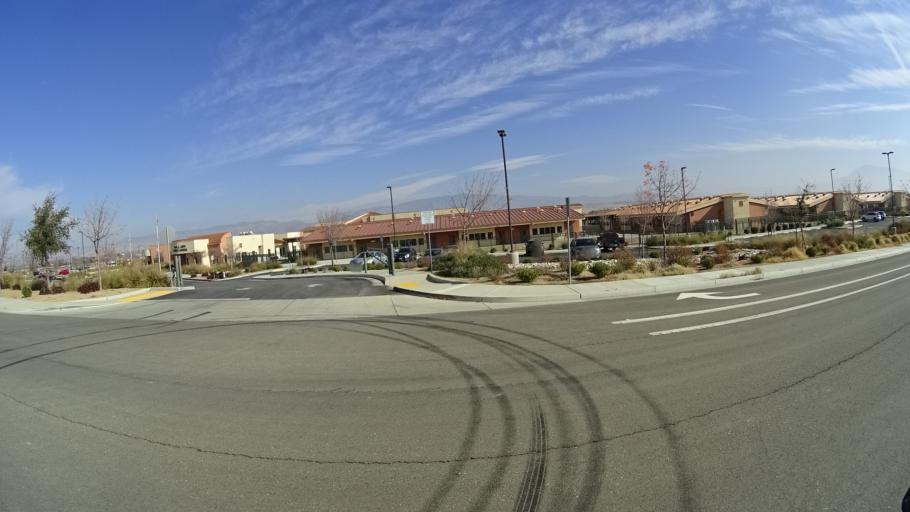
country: US
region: California
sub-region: Kern County
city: Bakersfield
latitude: 35.3905
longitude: -118.8962
